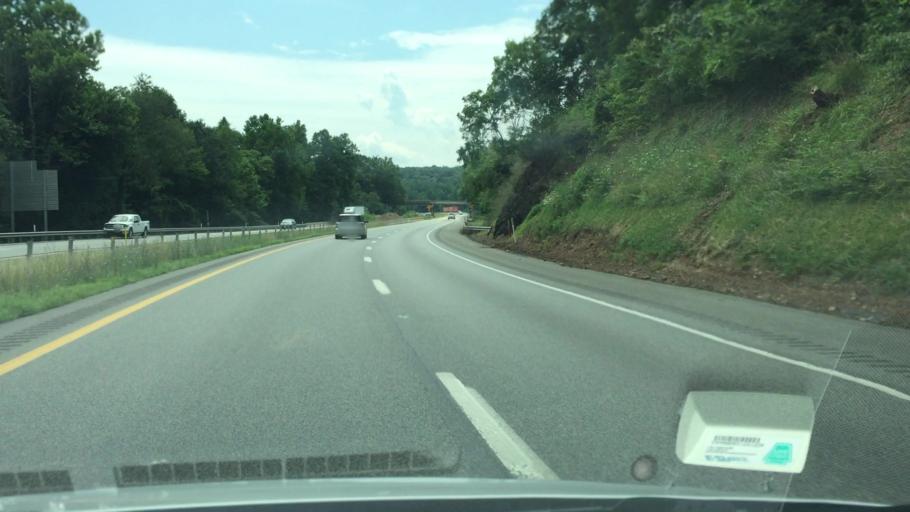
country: US
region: Maryland
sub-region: Washington County
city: Hancock
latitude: 39.7908
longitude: -78.2120
